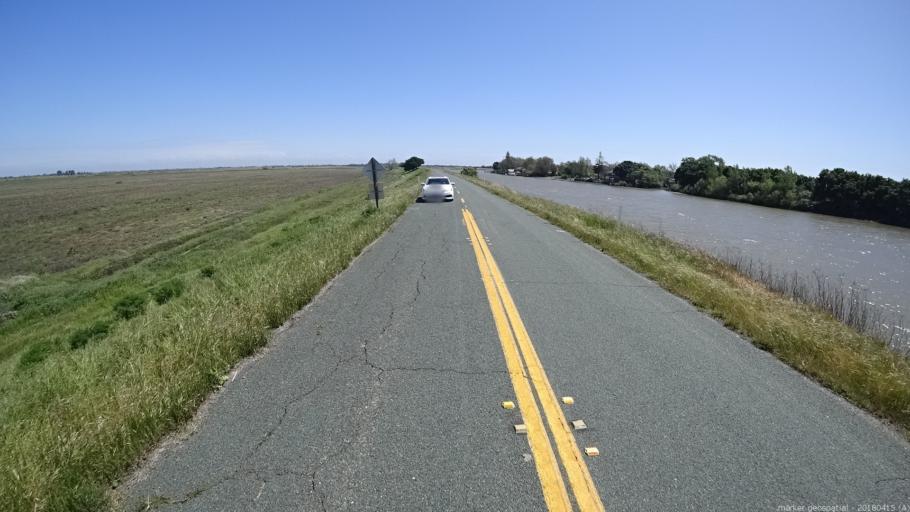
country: US
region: California
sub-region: Solano County
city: Rio Vista
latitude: 38.1737
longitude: -121.6457
